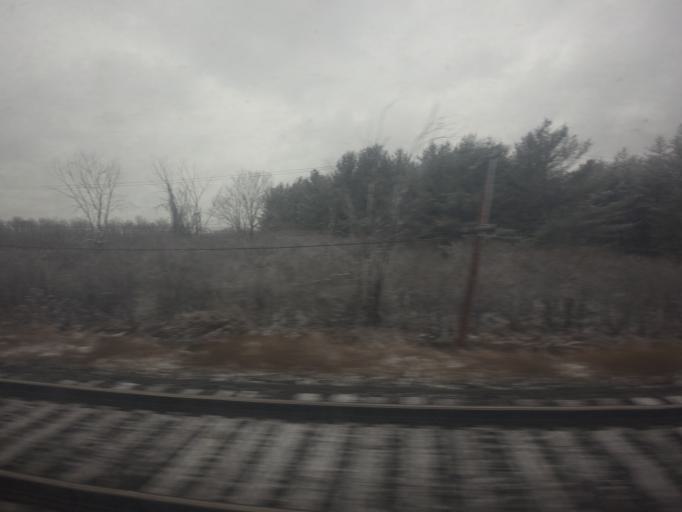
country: US
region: New York
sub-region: Jefferson County
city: Alexandria Bay
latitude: 44.4252
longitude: -75.9806
